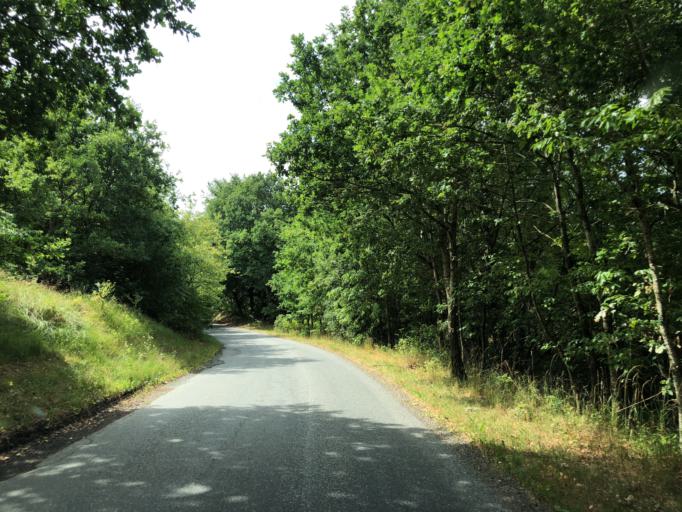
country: DK
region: South Denmark
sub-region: Vejle Kommune
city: Egtved
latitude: 55.6456
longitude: 9.2563
